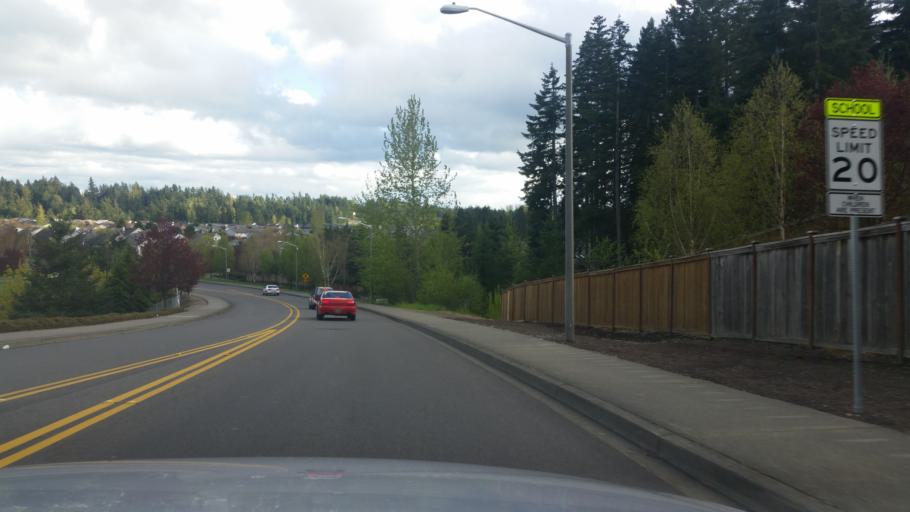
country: US
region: Washington
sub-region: Pierce County
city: Graham
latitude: 47.0860
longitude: -122.3098
